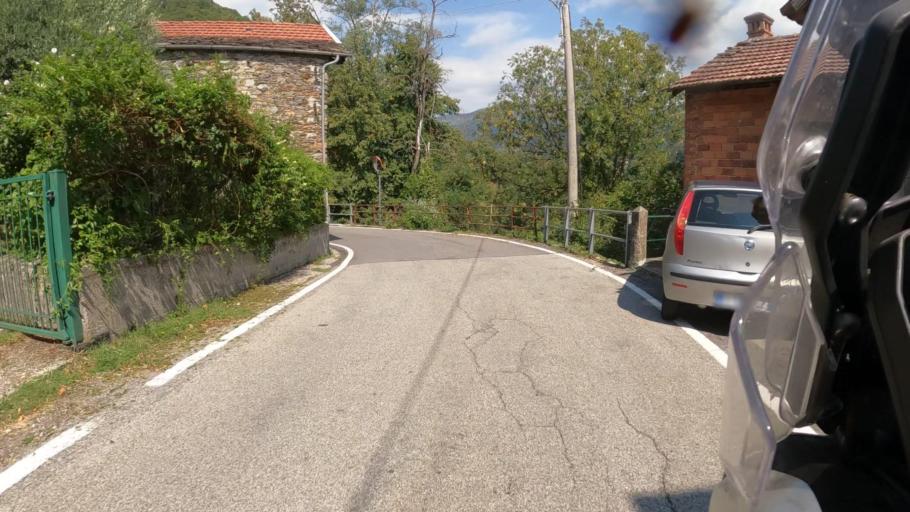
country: IT
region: Lombardy
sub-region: Provincia di Varese
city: Agra
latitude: 46.0563
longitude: 8.7740
